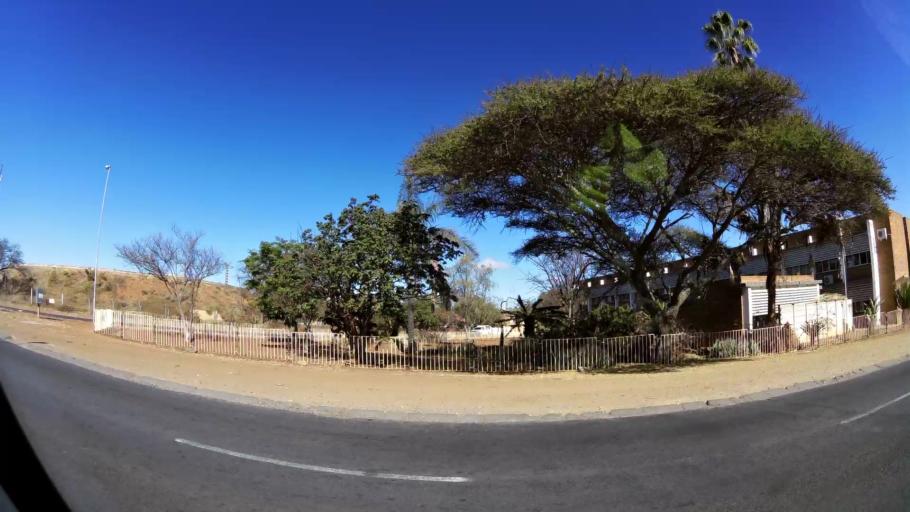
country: ZA
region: Limpopo
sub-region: Capricorn District Municipality
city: Polokwane
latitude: -23.8986
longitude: 29.4697
